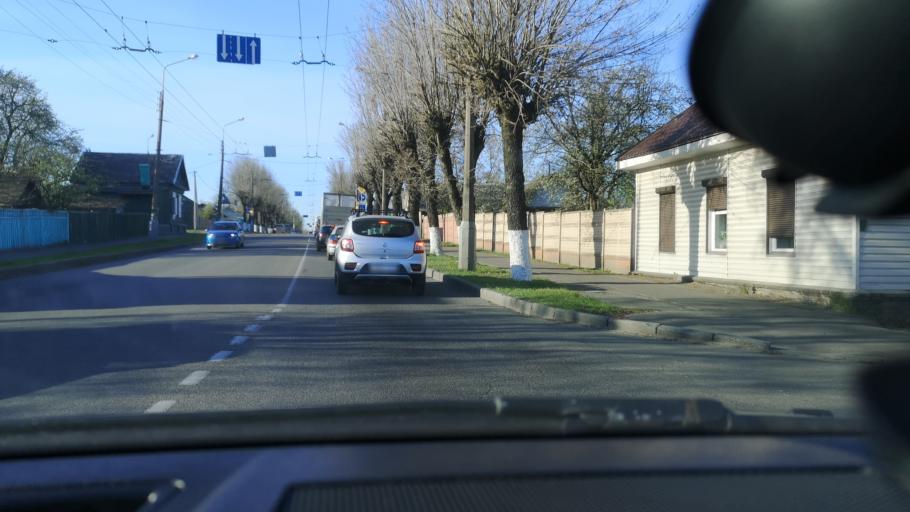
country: BY
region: Gomel
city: Gomel
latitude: 52.4298
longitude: 30.9751
